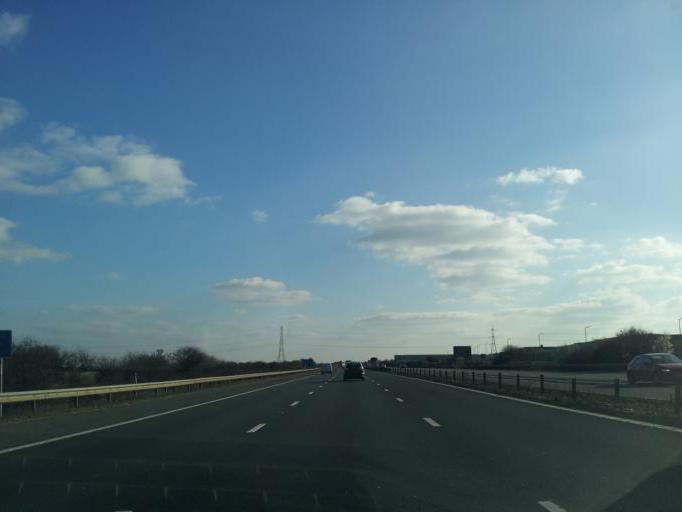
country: GB
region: England
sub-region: Somerset
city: Puriton
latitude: 51.1593
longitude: -2.9816
